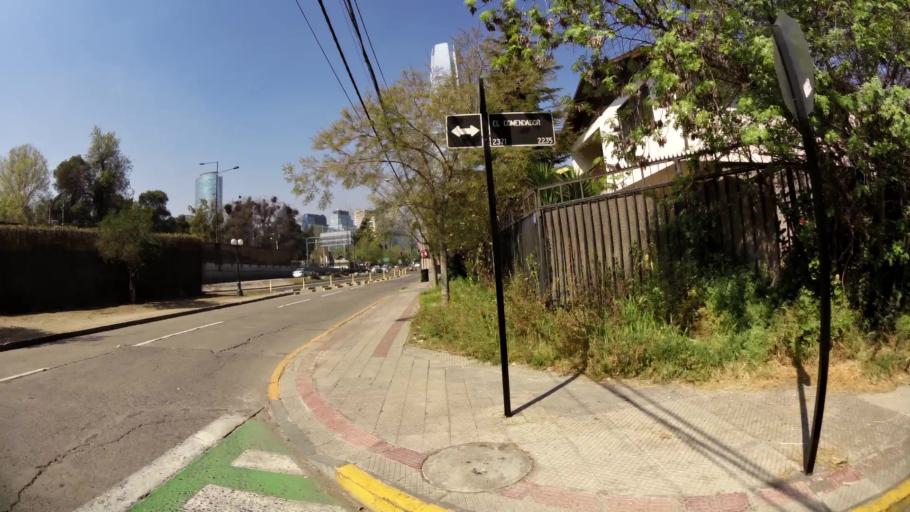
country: CL
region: Santiago Metropolitan
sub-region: Provincia de Santiago
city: Santiago
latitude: -33.4157
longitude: -70.6129
